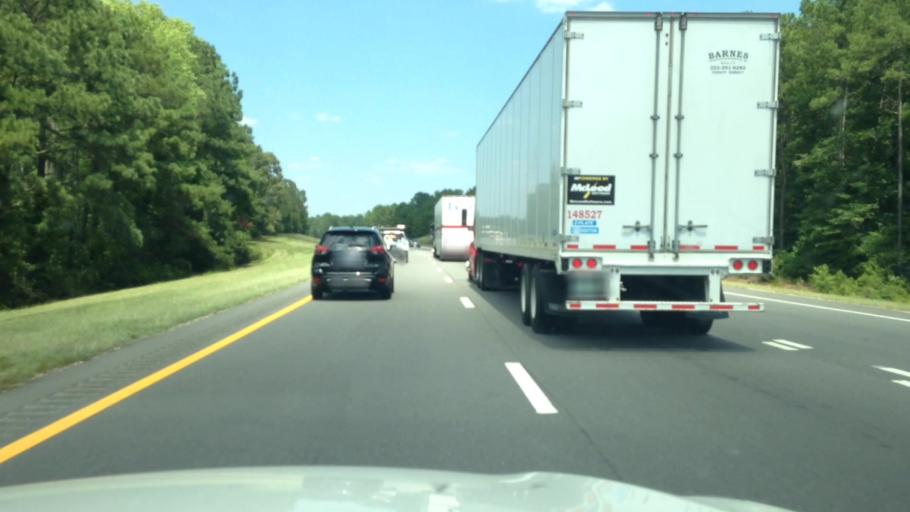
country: US
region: North Carolina
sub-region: Cumberland County
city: Hope Mills
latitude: 34.9405
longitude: -78.9165
